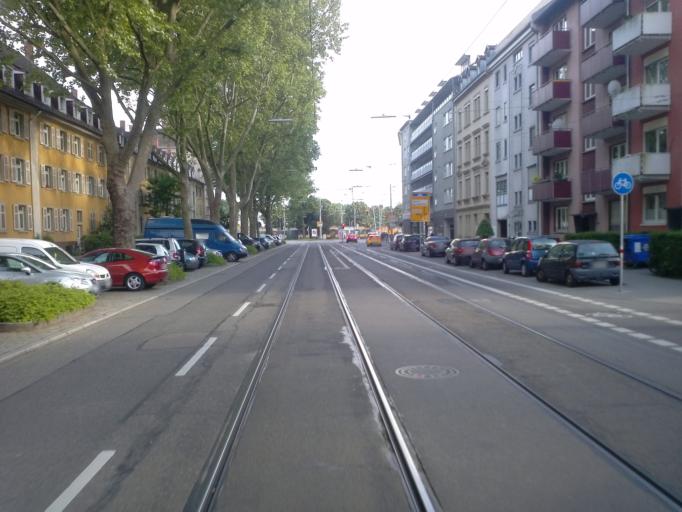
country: DE
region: Baden-Wuerttemberg
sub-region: Karlsruhe Region
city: Karlsruhe
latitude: 48.9982
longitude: 8.4106
